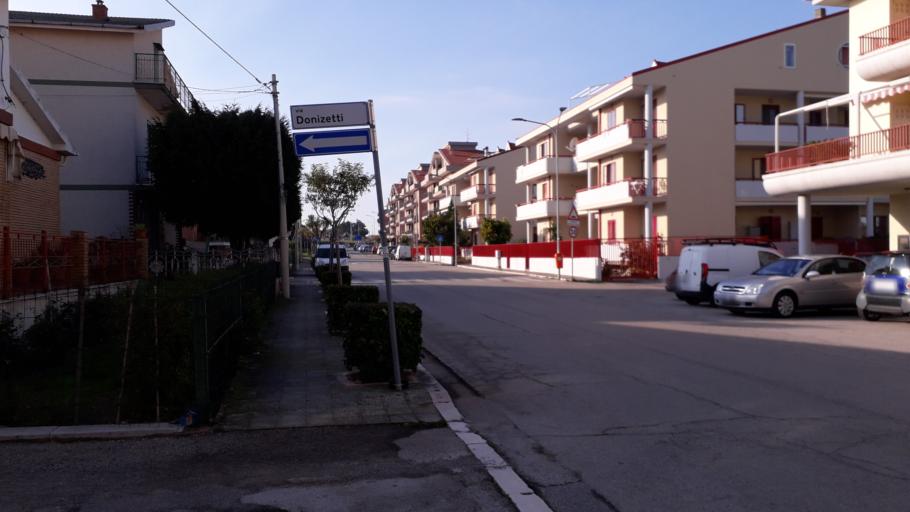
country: IT
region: Molise
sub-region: Provincia di Campobasso
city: Campomarino
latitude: 41.9547
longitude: 15.0311
